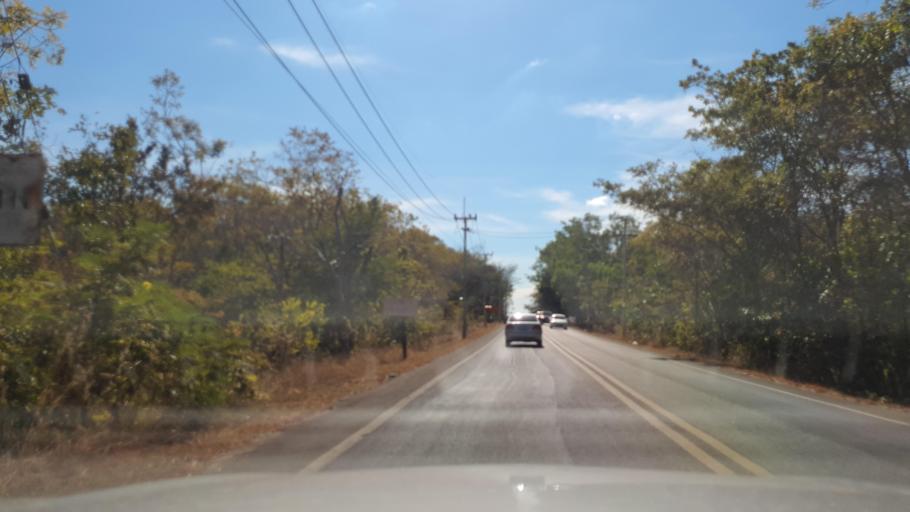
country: TH
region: Kalasin
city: Khao Wong
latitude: 16.7625
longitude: 104.1310
